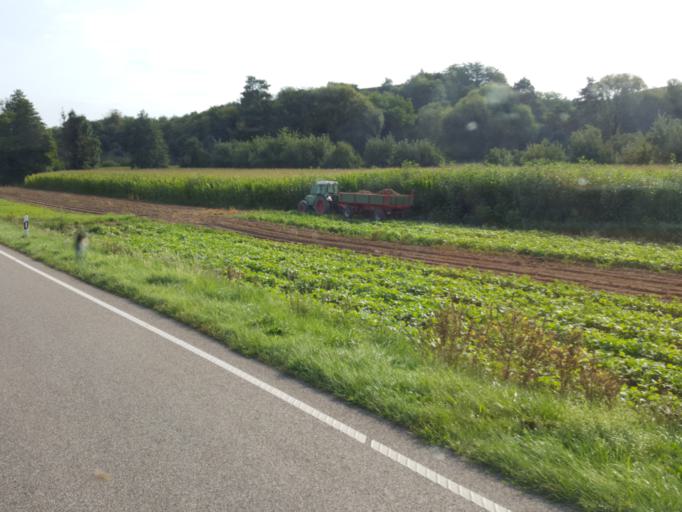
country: DE
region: Baden-Wuerttemberg
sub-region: Freiburg Region
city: Renchen
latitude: 48.5945
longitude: 8.0207
